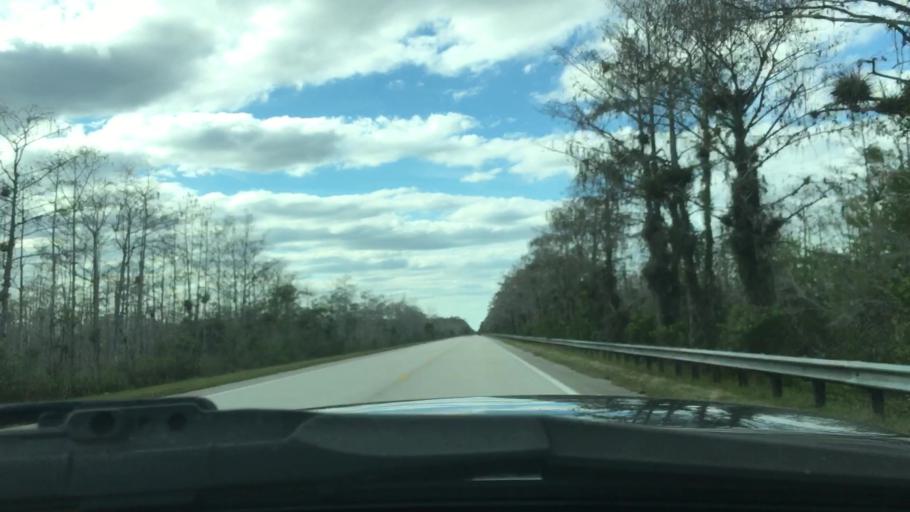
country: US
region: Florida
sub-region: Miami-Dade County
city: Kendall West
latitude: 25.8498
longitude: -80.9647
